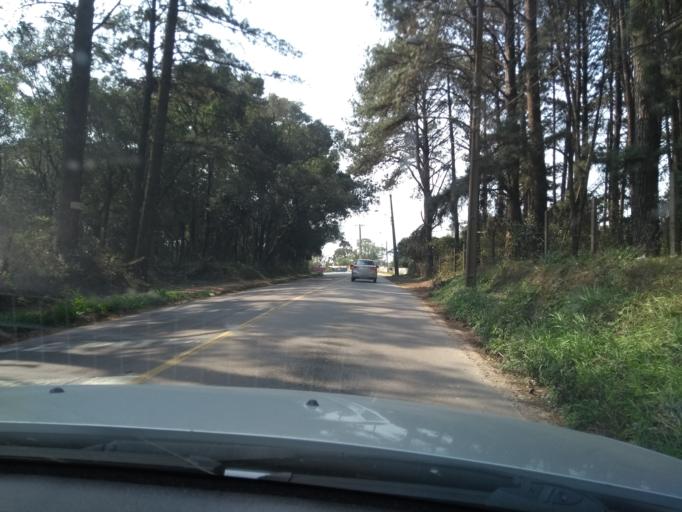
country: BR
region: Parana
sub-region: Araucaria
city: Araucaria
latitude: -25.6045
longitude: -49.3275
